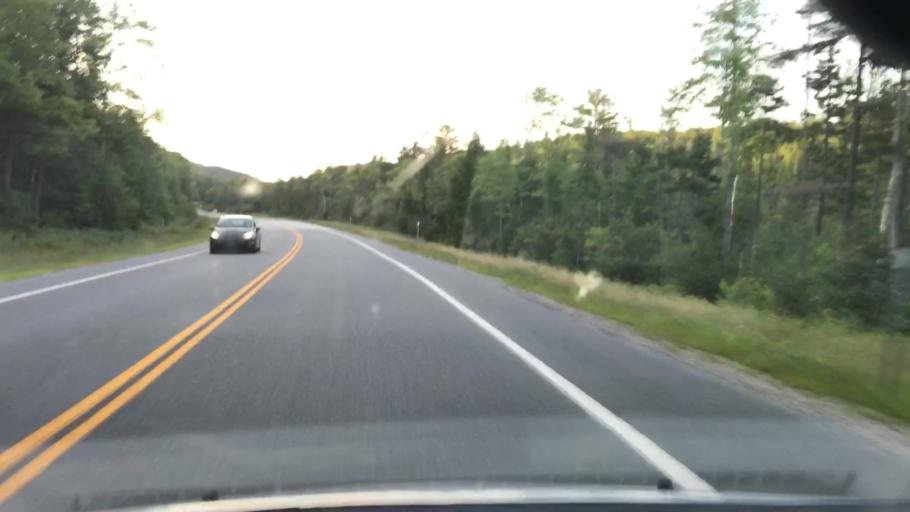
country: US
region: New Hampshire
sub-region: Grafton County
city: Rumney
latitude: 43.9630
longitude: -71.8853
